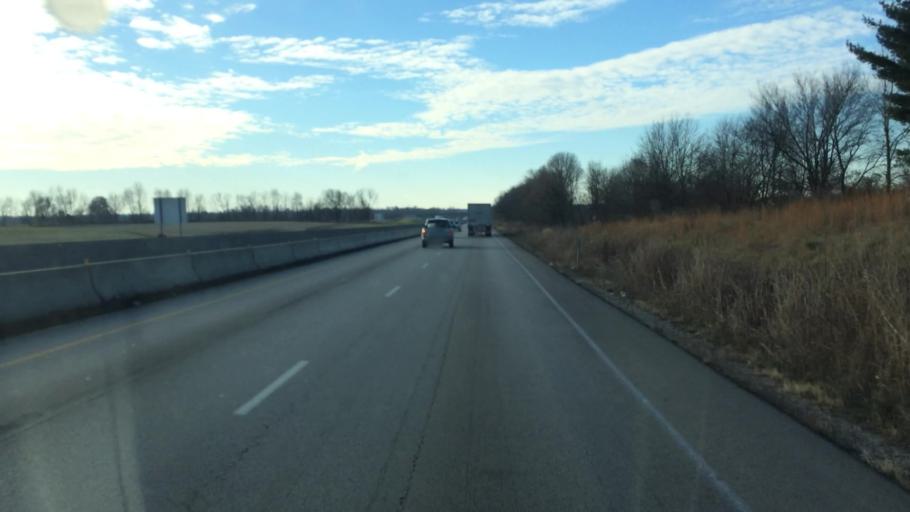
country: US
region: Kentucky
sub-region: Hardin County
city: Elizabethtown
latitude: 37.5805
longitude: -85.8723
